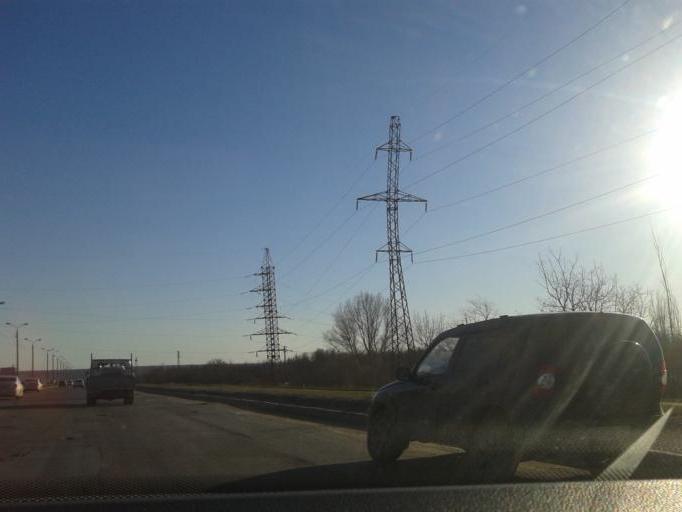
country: RU
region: Volgograd
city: Volgograd
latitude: 48.7458
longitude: 44.4658
